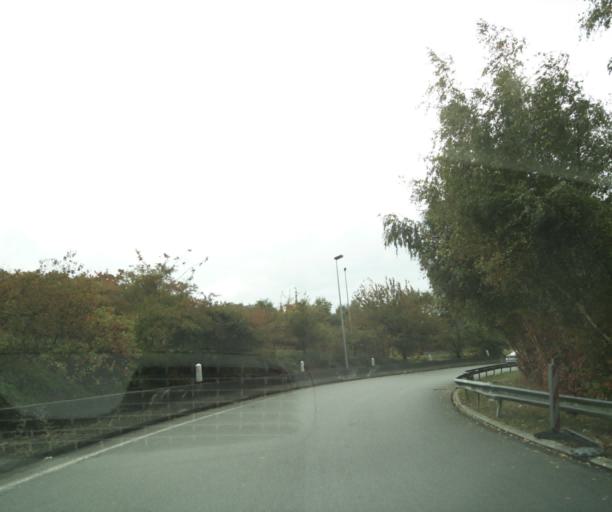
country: FR
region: Nord-Pas-de-Calais
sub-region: Departement du Nord
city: Wasquehal
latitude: 50.6799
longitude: 3.1271
